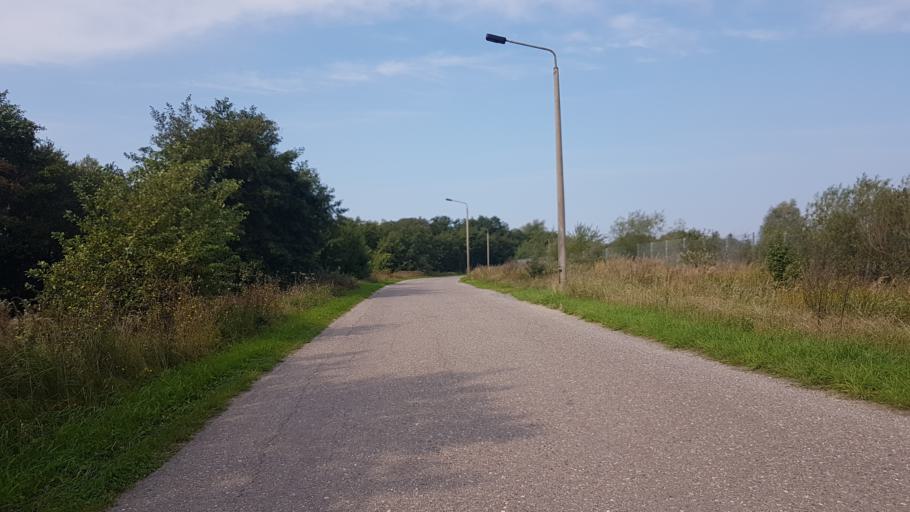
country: DE
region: Mecklenburg-Vorpommern
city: Sagard
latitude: 54.4946
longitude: 13.5548
